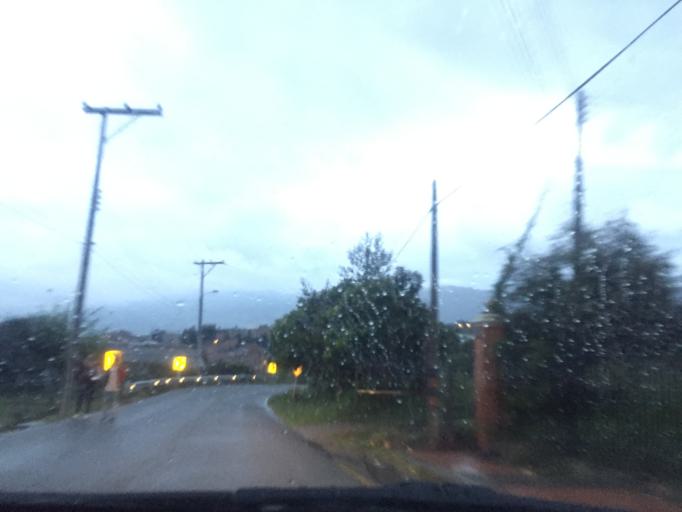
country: CO
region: Cundinamarca
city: Cogua
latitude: 5.0666
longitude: -73.9756
